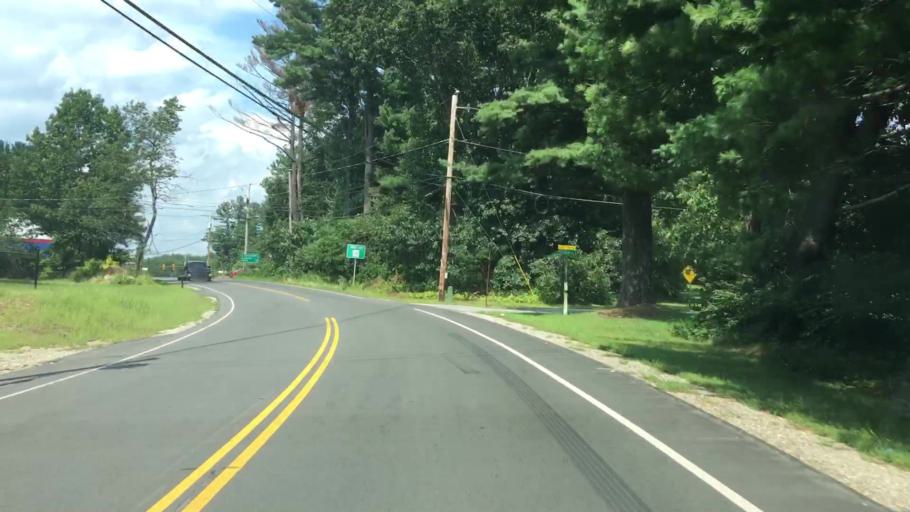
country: US
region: New Hampshire
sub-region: Rockingham County
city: Windham
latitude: 42.8005
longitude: -71.3518
